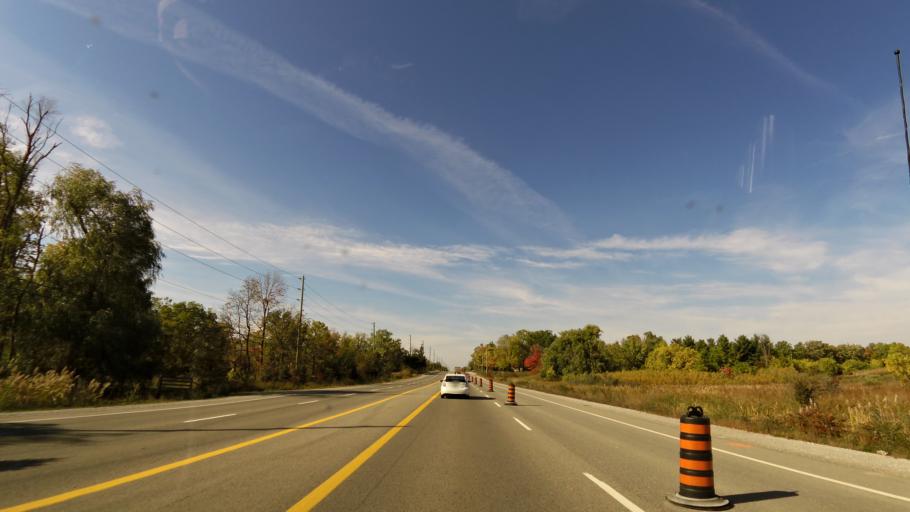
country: CA
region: Ontario
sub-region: Halton
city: Milton
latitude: 43.5454
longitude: -79.7946
